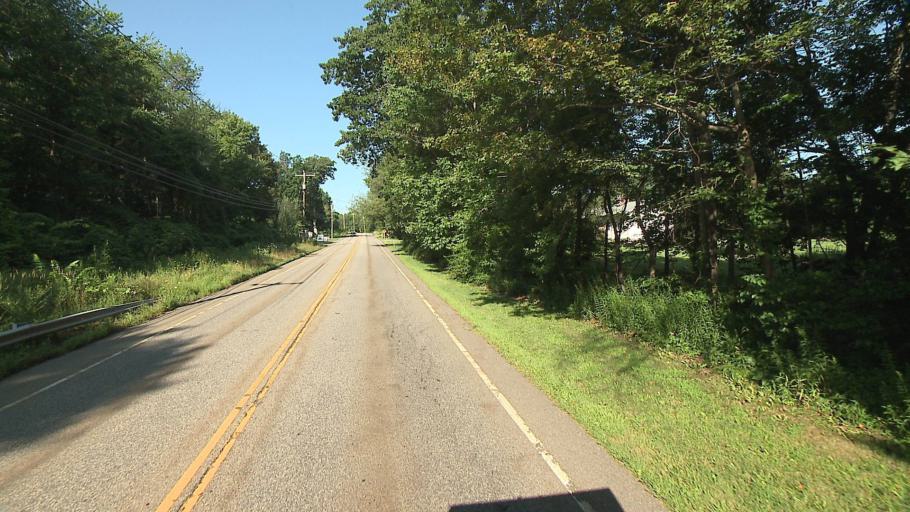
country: US
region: Connecticut
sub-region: Litchfield County
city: Northwest Harwinton
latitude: 41.7772
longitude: -73.0053
